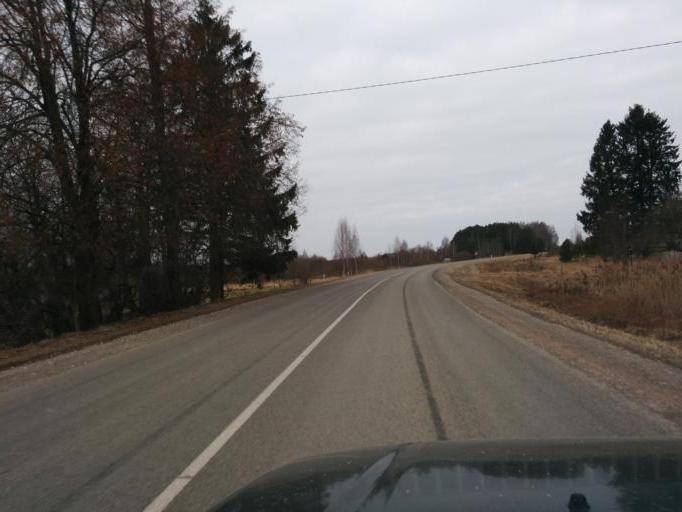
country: LV
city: Tireli
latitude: 56.8340
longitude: 23.5950
